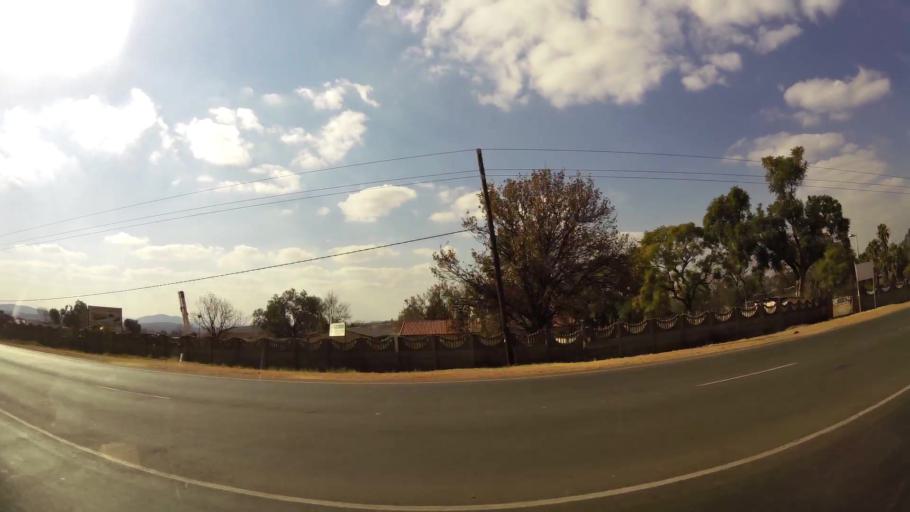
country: ZA
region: Gauteng
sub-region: West Rand District Municipality
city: Muldersdriseloop
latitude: -26.0607
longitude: 27.8299
